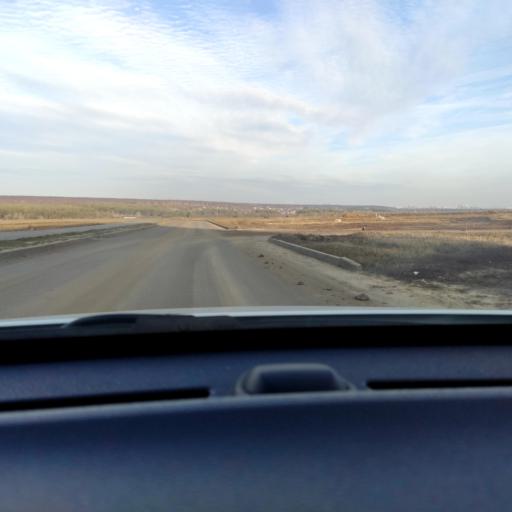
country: RU
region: Voronezj
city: Shilovo
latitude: 51.5721
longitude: 39.1212
